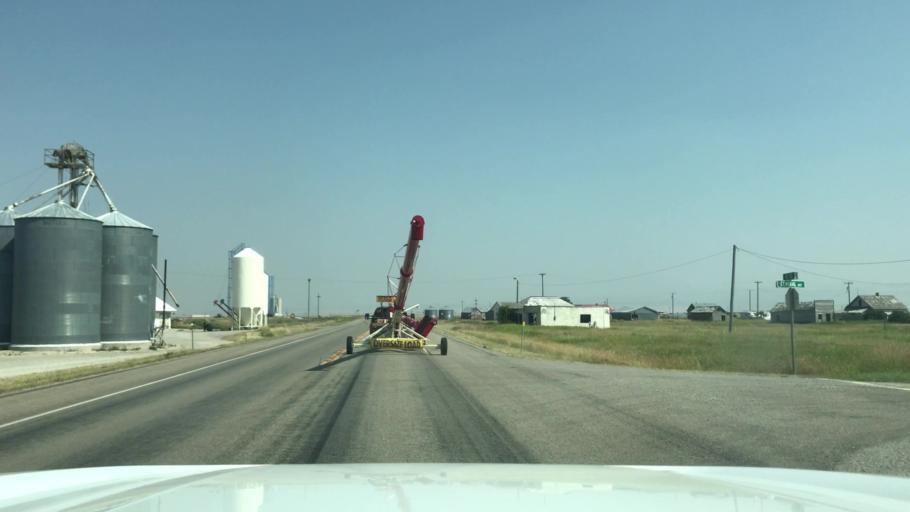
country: US
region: Montana
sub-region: Judith Basin County
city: Stanford
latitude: 47.0544
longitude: -109.9107
